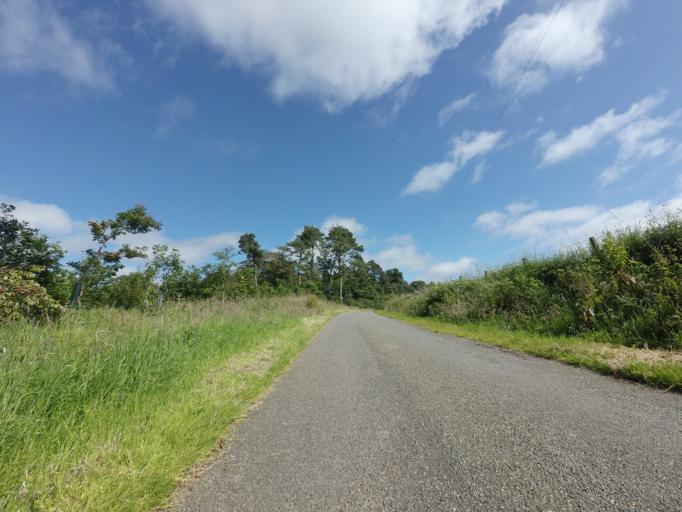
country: GB
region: Scotland
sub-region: Aberdeenshire
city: Turriff
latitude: 57.5837
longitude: -2.5062
